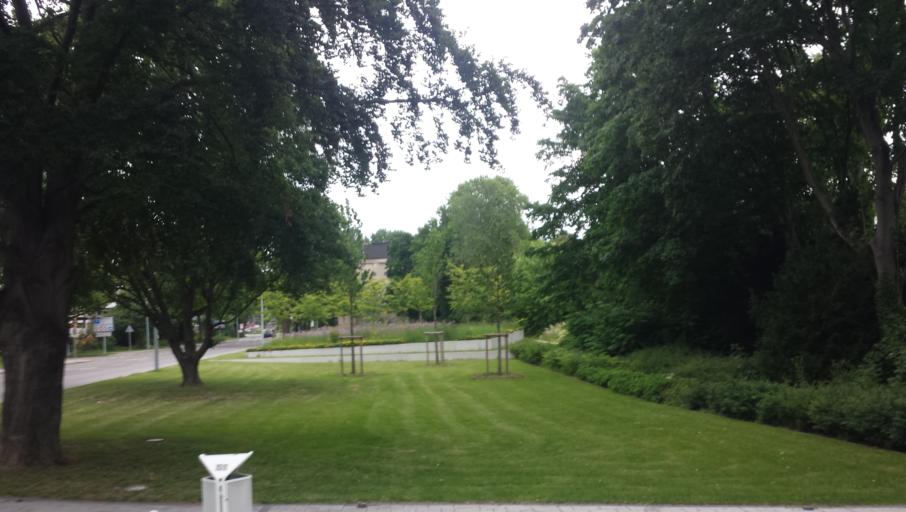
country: DE
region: Rheinland-Pfalz
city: Ludwigshafen am Rhein
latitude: 49.4931
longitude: 8.4289
